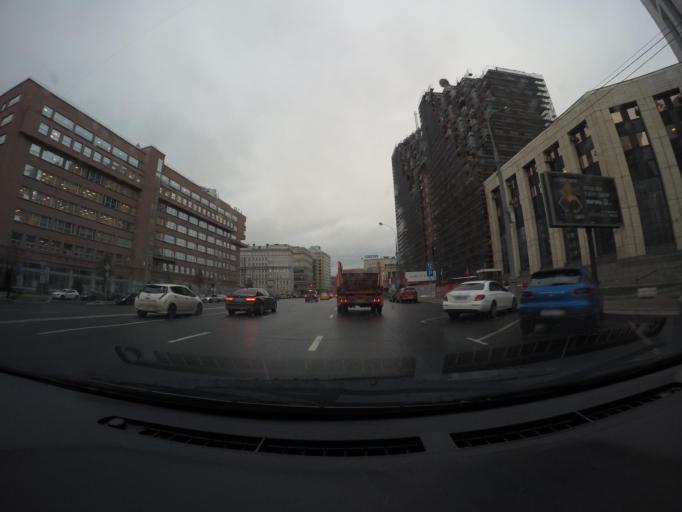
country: RU
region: Moscow
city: Moscow
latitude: 55.7716
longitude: 37.6454
